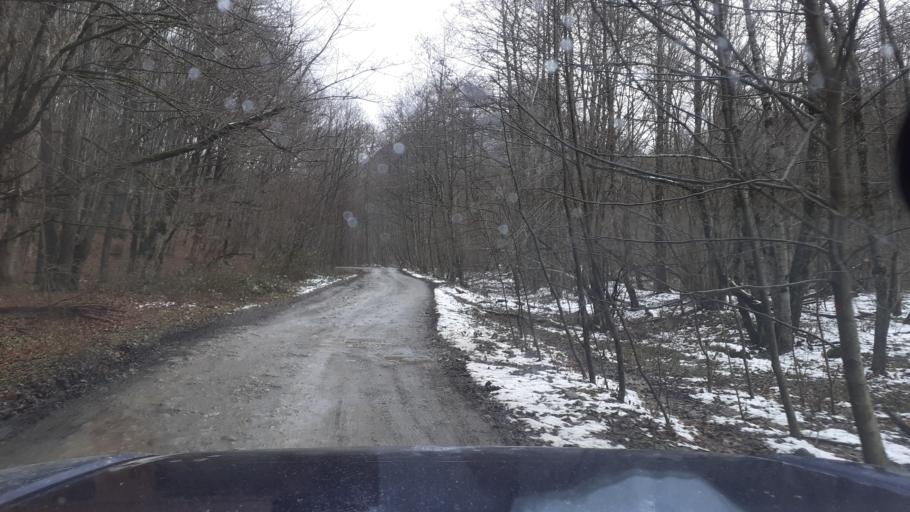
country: RU
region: Krasnodarskiy
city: Neftegorsk
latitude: 44.0704
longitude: 39.7128
